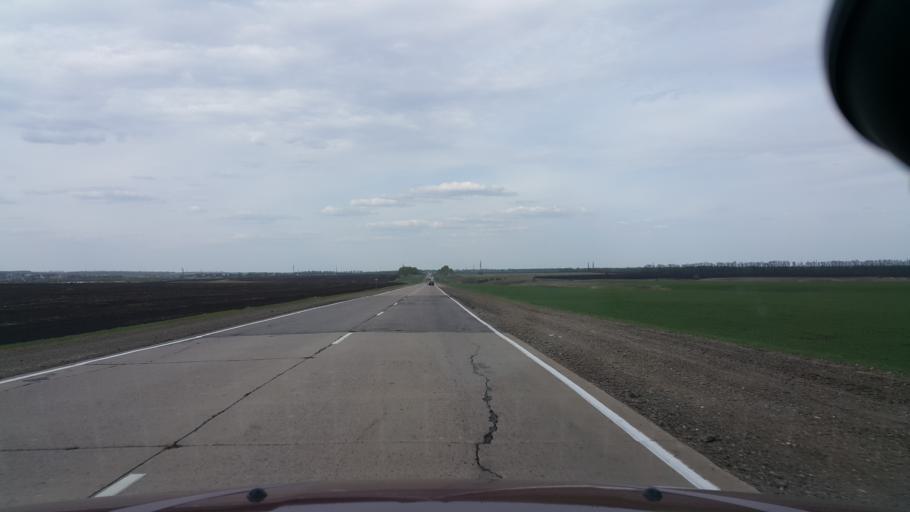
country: RU
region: Tambov
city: Pokrovo-Prigorodnoye
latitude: 52.6240
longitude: 41.3428
